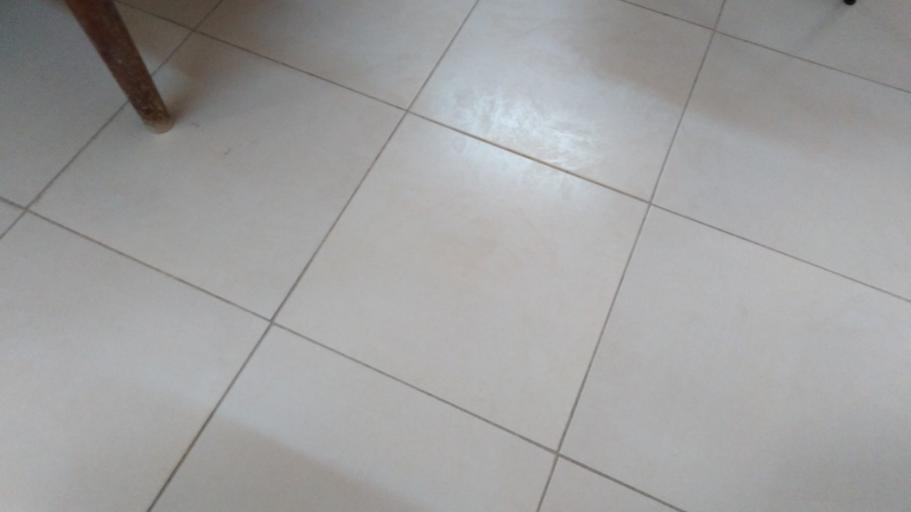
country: TN
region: Qabis
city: Gabes
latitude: 33.9605
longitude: 9.9972
